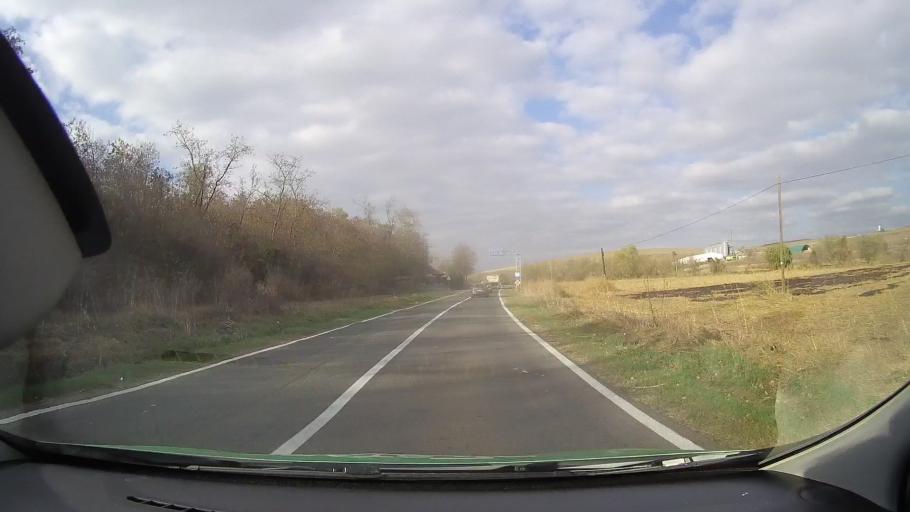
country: RO
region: Tulcea
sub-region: Comuna Ciucurova
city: Ciucurova
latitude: 44.9245
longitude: 28.4494
